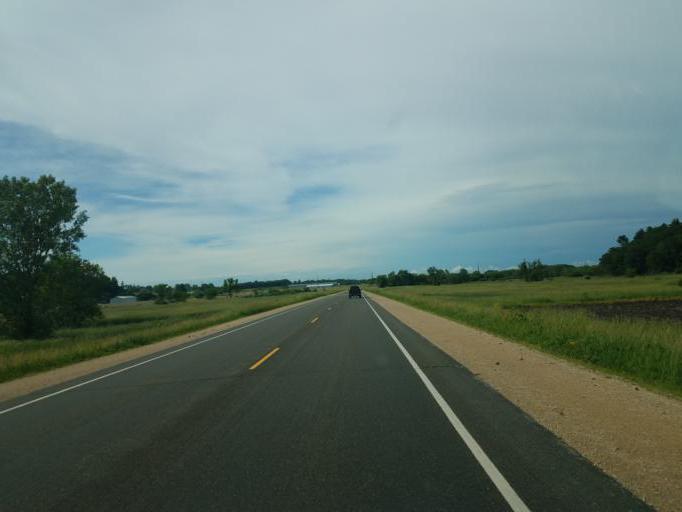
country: US
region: Wisconsin
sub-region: Monroe County
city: Tomah
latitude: 43.9420
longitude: -90.5032
